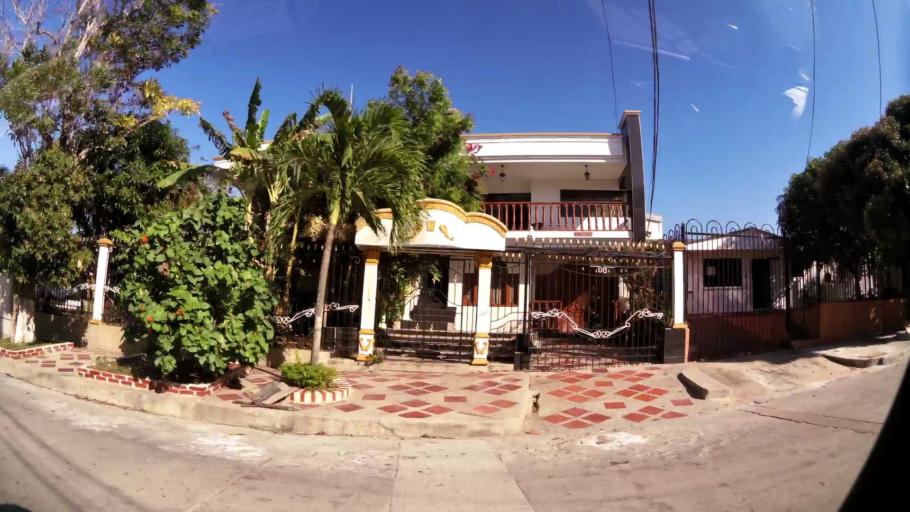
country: CO
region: Atlantico
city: Barranquilla
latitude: 10.9978
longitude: -74.8276
